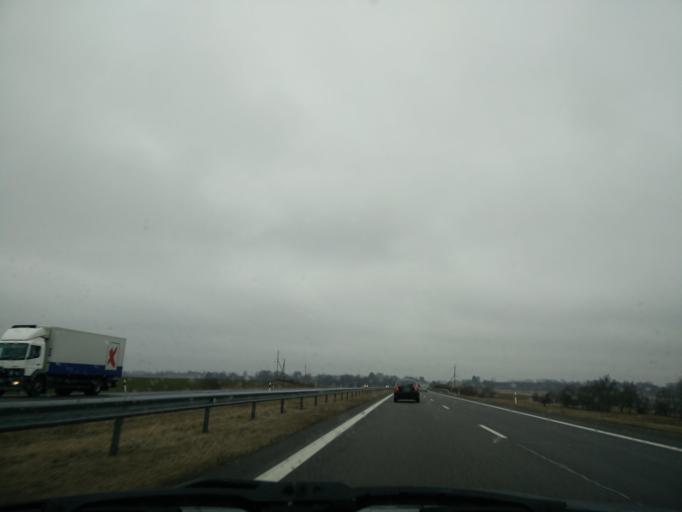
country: LT
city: Skaudvile
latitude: 55.4400
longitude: 22.7307
